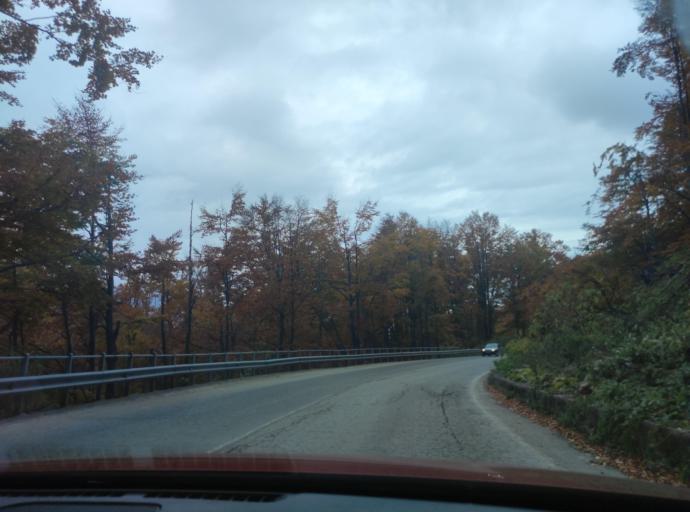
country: BG
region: Montana
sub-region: Obshtina Berkovitsa
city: Berkovitsa
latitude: 43.1274
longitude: 23.1398
